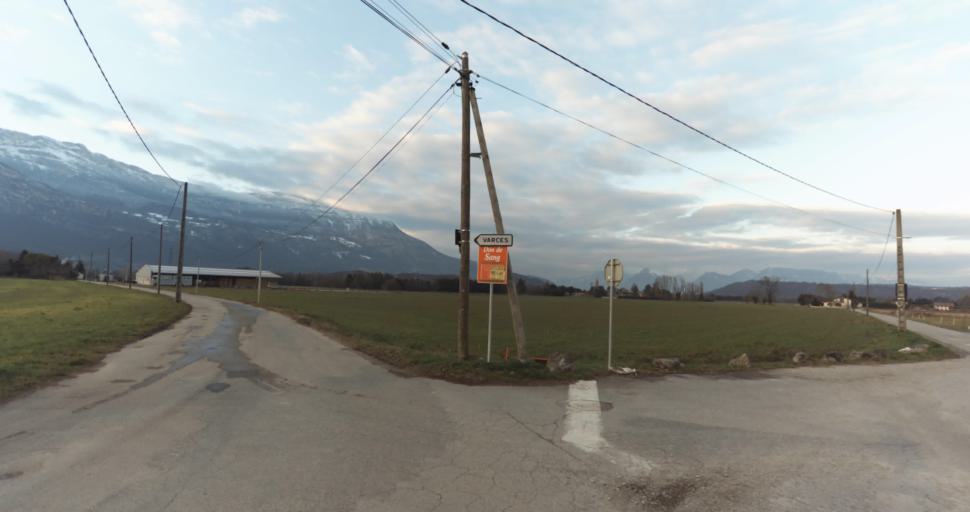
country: FR
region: Rhone-Alpes
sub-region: Departement de l'Isere
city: Allieres-et-Risset
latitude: 45.0782
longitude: 5.7020
